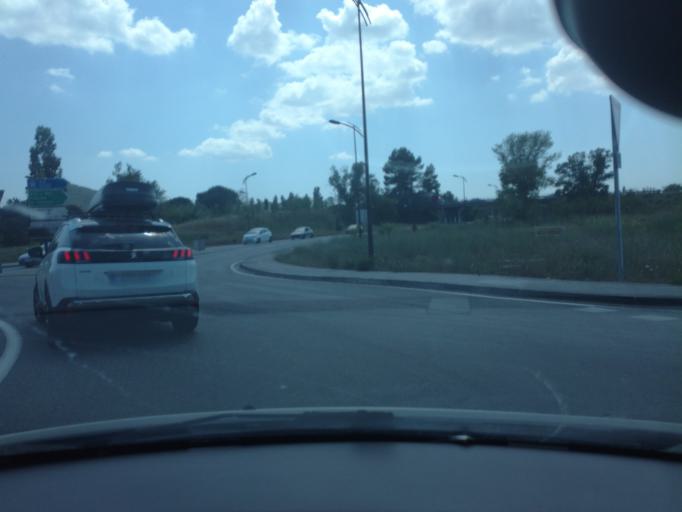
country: FR
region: Provence-Alpes-Cote d'Azur
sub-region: Departement du Var
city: Le Muy
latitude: 43.4676
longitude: 6.5473
